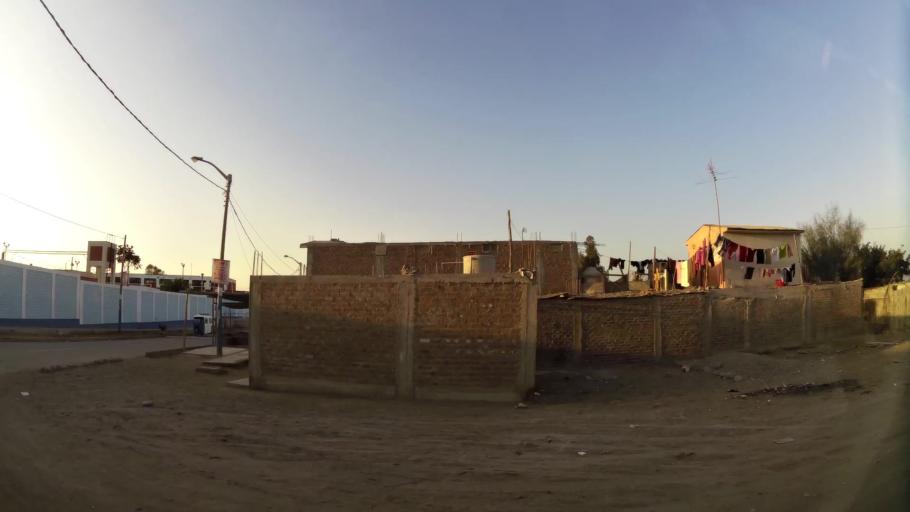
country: PE
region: Ica
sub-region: Provincia de Pisco
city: Villa Tupac Amaru
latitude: -13.7009
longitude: -76.1532
